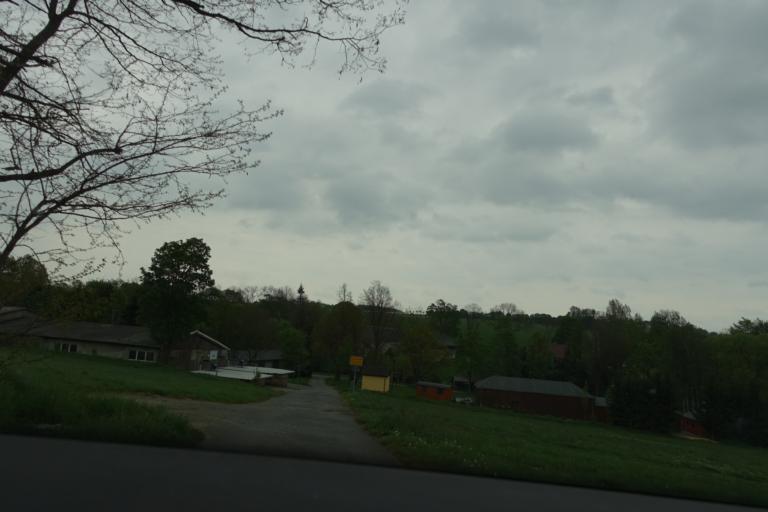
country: DE
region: Saxony
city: Eppendorf
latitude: 50.8198
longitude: 13.2628
